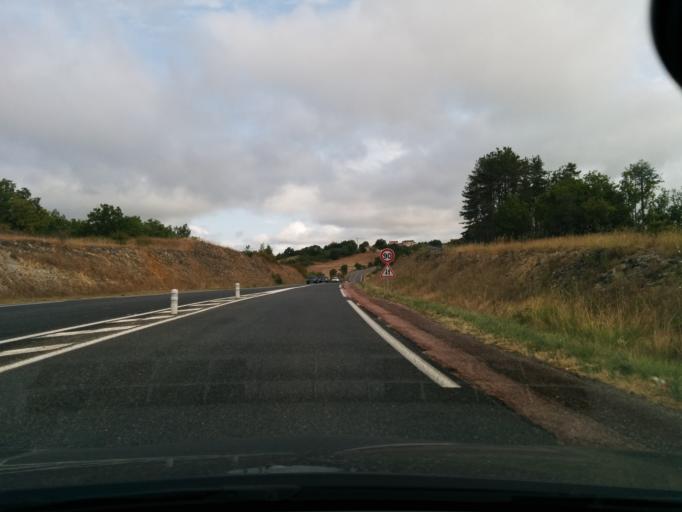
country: FR
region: Midi-Pyrenees
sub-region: Departement du Lot
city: Pradines
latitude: 44.5126
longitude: 1.4439
